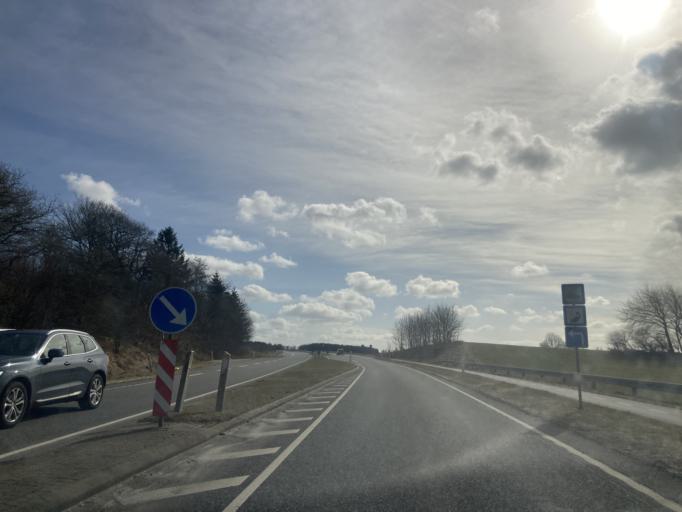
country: DK
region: Central Jutland
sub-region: Hedensted Kommune
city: Torring
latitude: 55.9910
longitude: 9.3882
